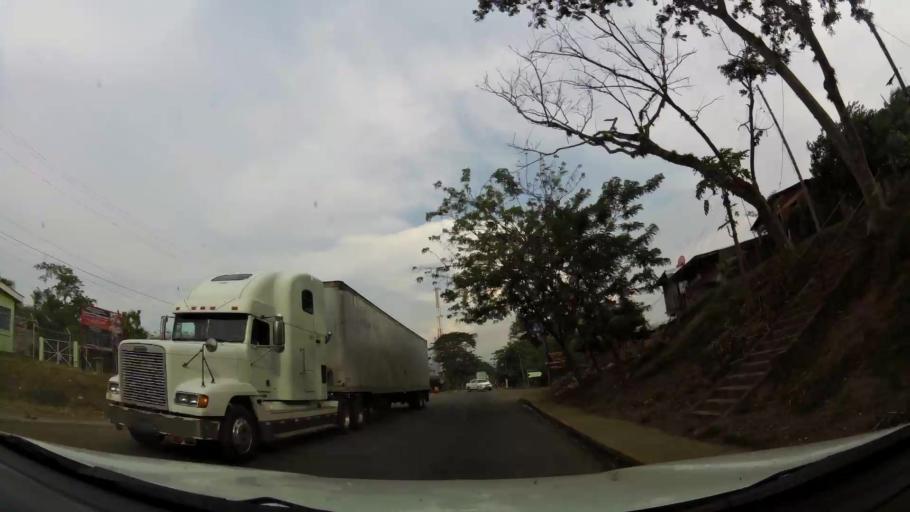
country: NI
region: Rivas
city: Cardenas
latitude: 11.2481
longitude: -85.6272
